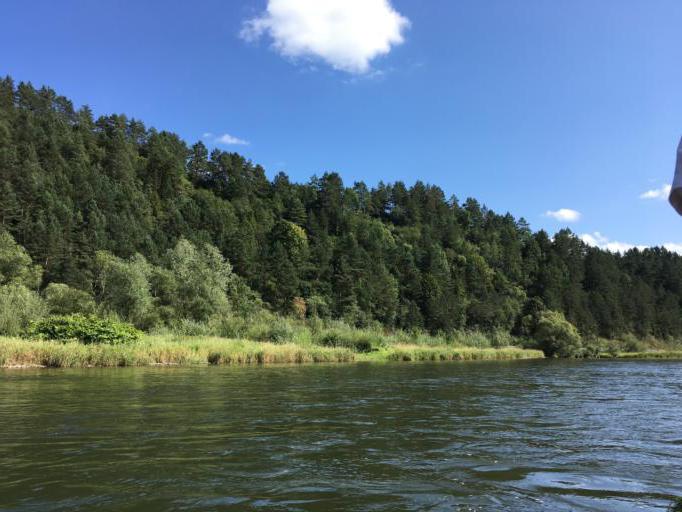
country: PL
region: Lesser Poland Voivodeship
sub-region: Powiat nowotarski
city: Kroscienko nad Dunajcem
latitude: 49.4046
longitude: 20.3797
